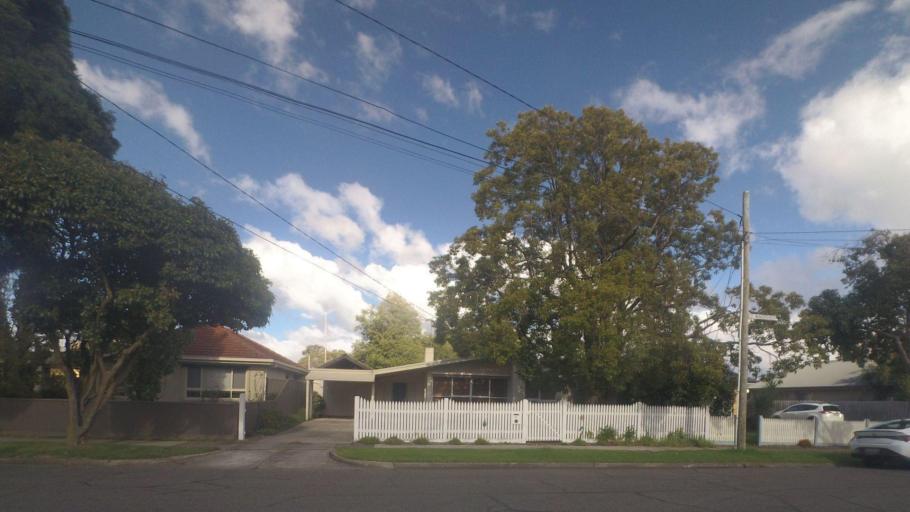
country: AU
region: Victoria
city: Forest Hill
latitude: -37.8426
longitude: 145.1819
